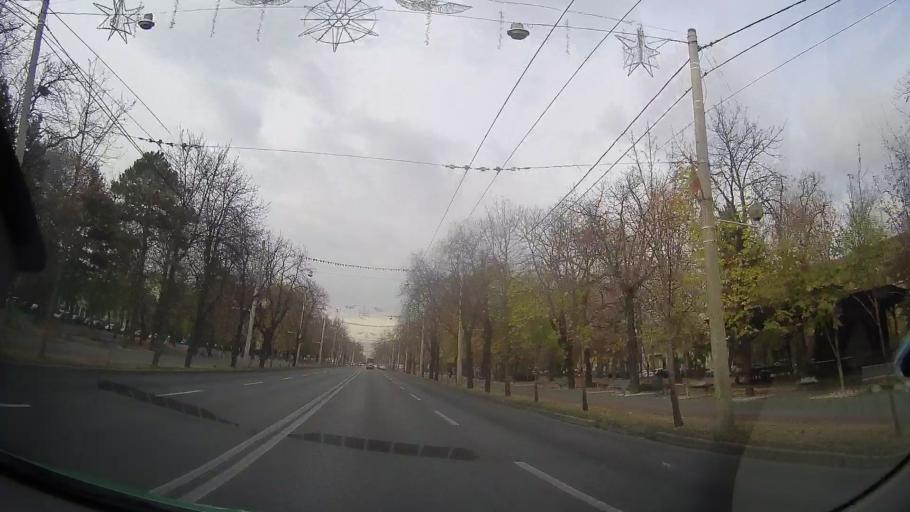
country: RO
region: Prahova
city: Ploiesti
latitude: 44.9315
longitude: 26.0276
